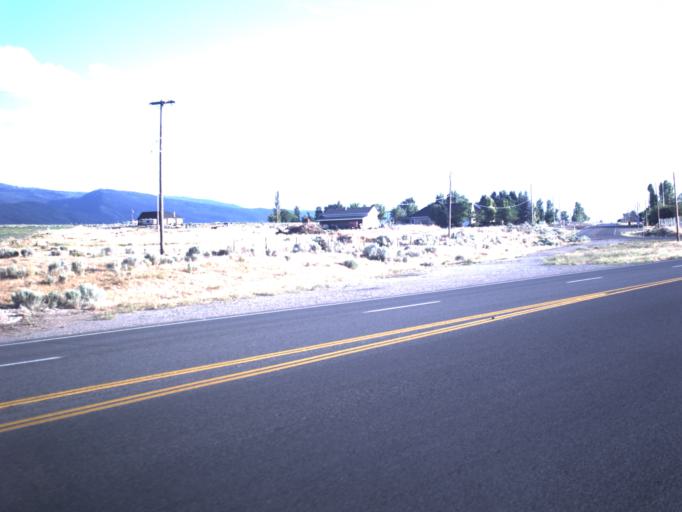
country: US
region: Utah
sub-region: Sanpete County
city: Mount Pleasant
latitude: 39.5300
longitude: -111.4663
